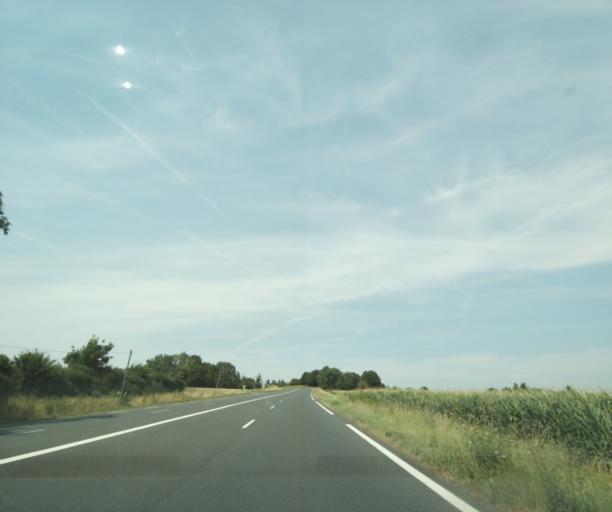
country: FR
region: Centre
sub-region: Departement d'Indre-et-Loire
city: La Celle-Saint-Avant
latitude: 47.0556
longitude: 0.6154
